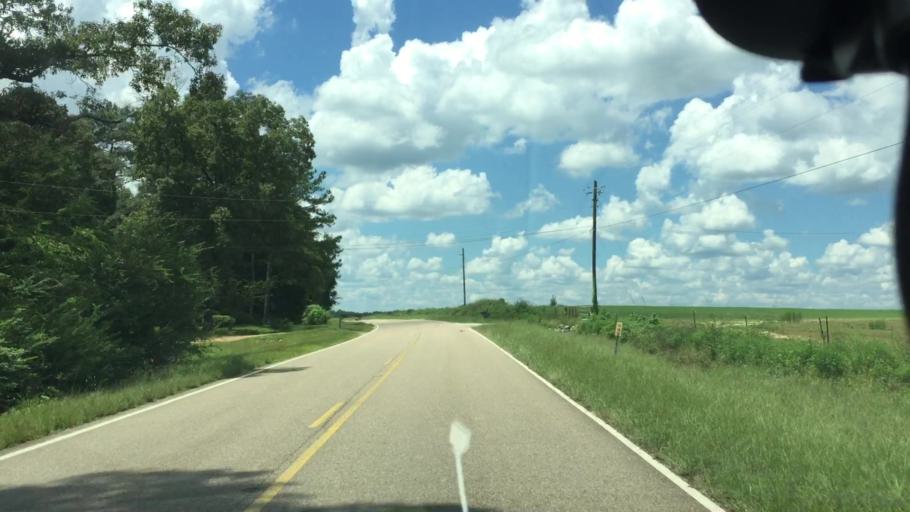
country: US
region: Alabama
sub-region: Coffee County
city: New Brockton
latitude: 31.4162
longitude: -85.8791
